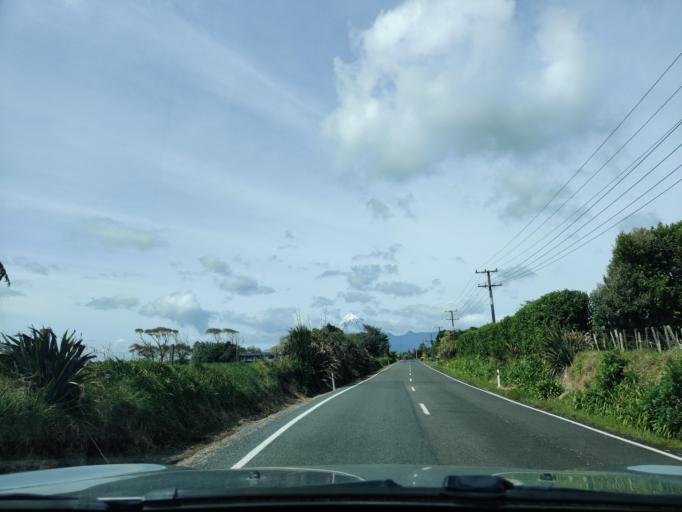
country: NZ
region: Taranaki
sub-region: New Plymouth District
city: New Plymouth
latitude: -39.1015
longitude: 174.1002
